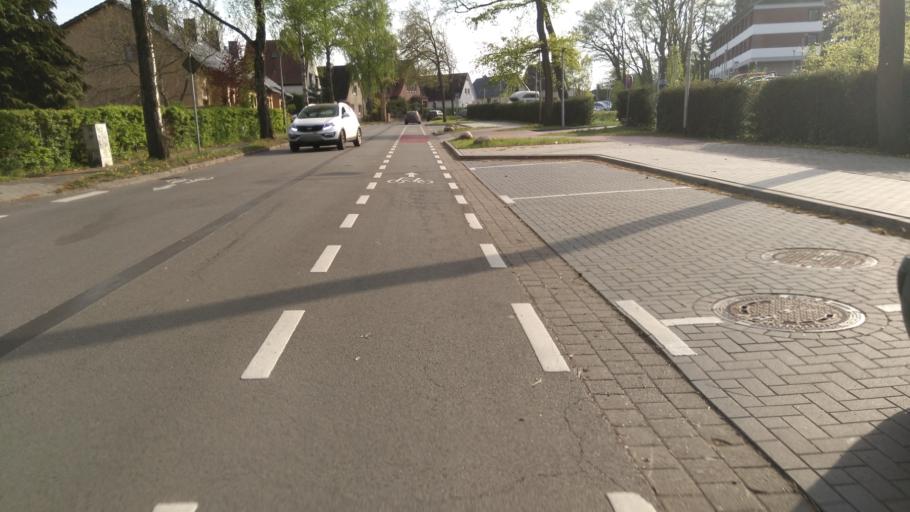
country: DE
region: Lower Saxony
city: Buxtehude
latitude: 53.4614
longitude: 9.6771
